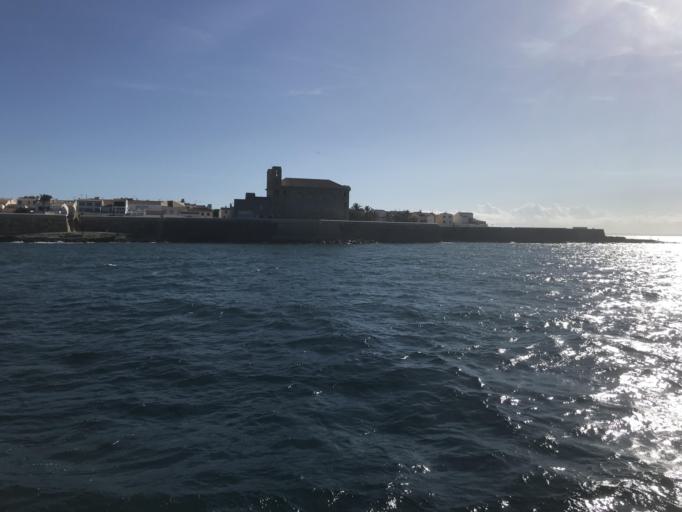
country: ES
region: Valencia
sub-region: Provincia de Alicante
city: Santa Pola
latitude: 38.1690
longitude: -0.4813
